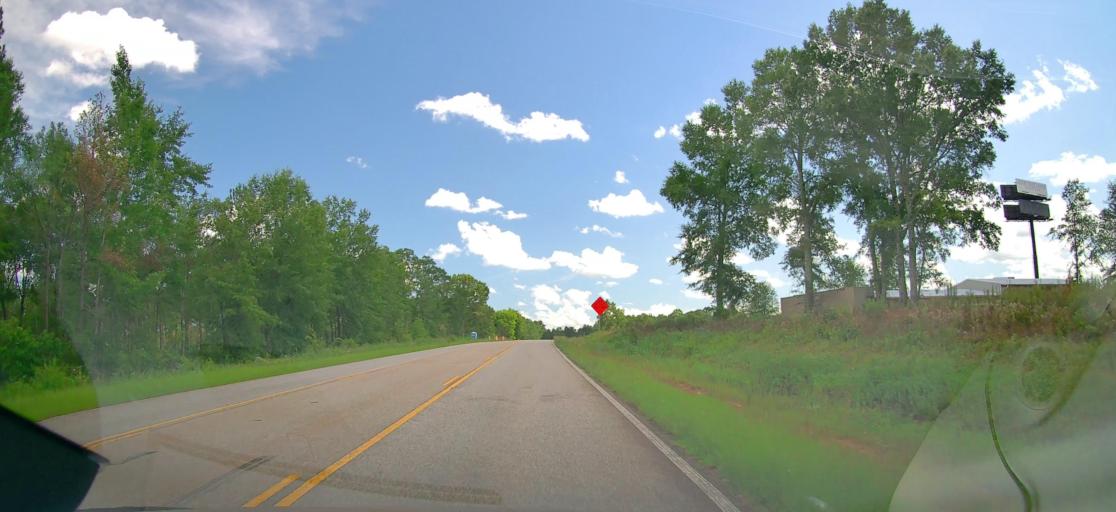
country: US
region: Georgia
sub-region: Peach County
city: Byron
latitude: 32.6043
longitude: -83.7406
